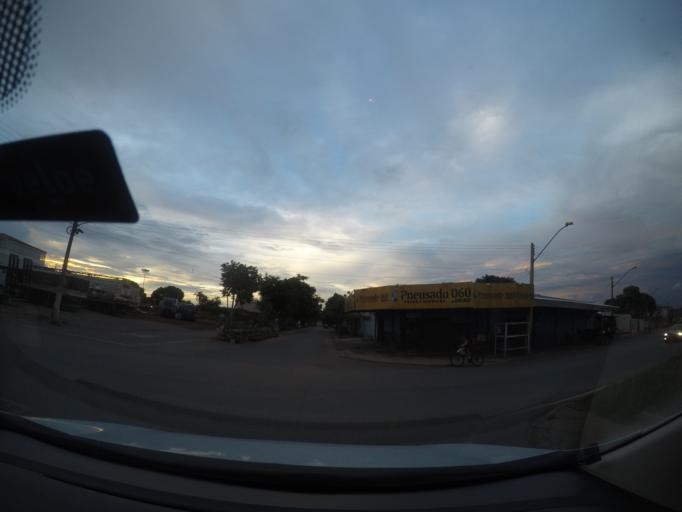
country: BR
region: Goias
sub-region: Goiania
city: Goiania
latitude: -16.7213
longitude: -49.3733
